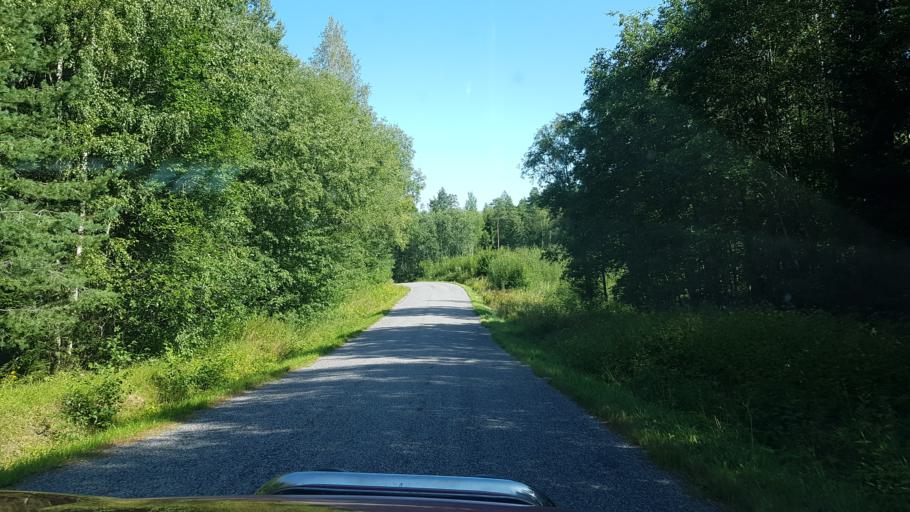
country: EE
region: Vorumaa
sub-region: Voru linn
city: Voru
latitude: 57.7091
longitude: 27.1925
